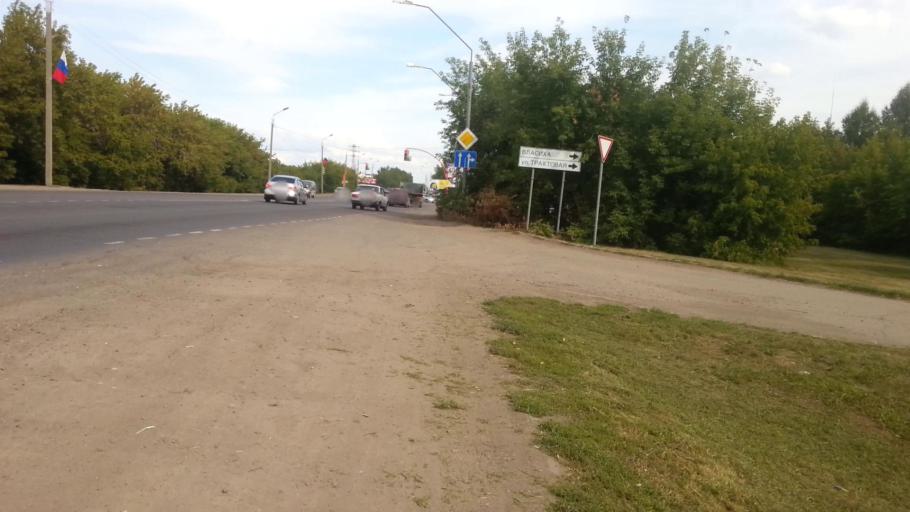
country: RU
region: Altai Krai
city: Novosilikatnyy
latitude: 53.3495
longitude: 83.6184
